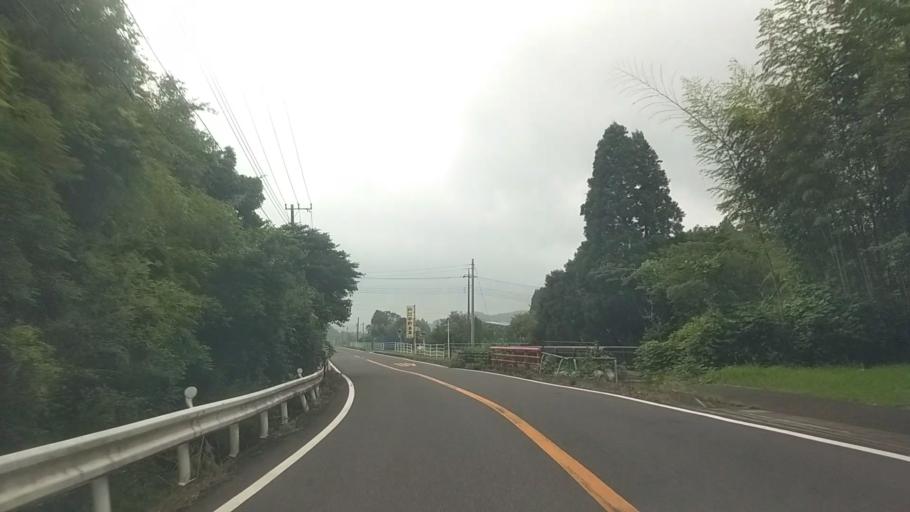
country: JP
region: Chiba
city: Katsuura
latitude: 35.2529
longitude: 140.2245
